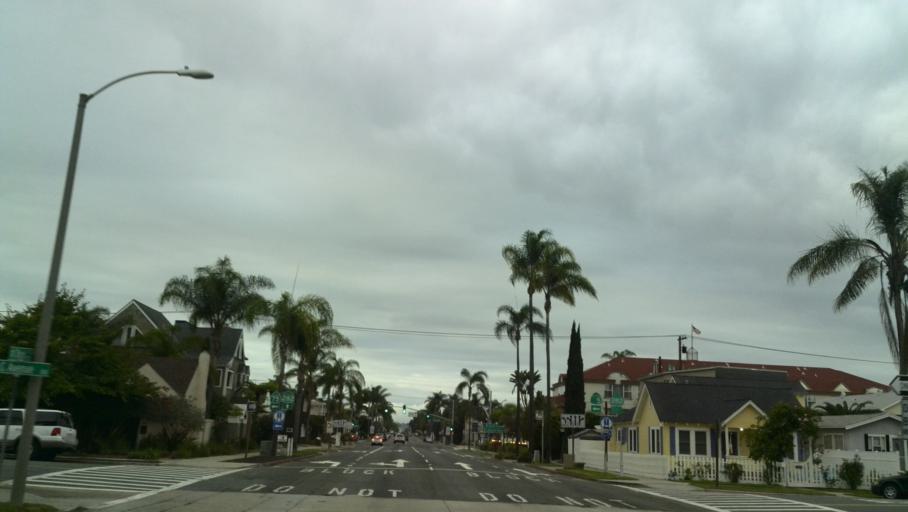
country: US
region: California
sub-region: San Diego County
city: Coronado
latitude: 32.6953
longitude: -117.1726
